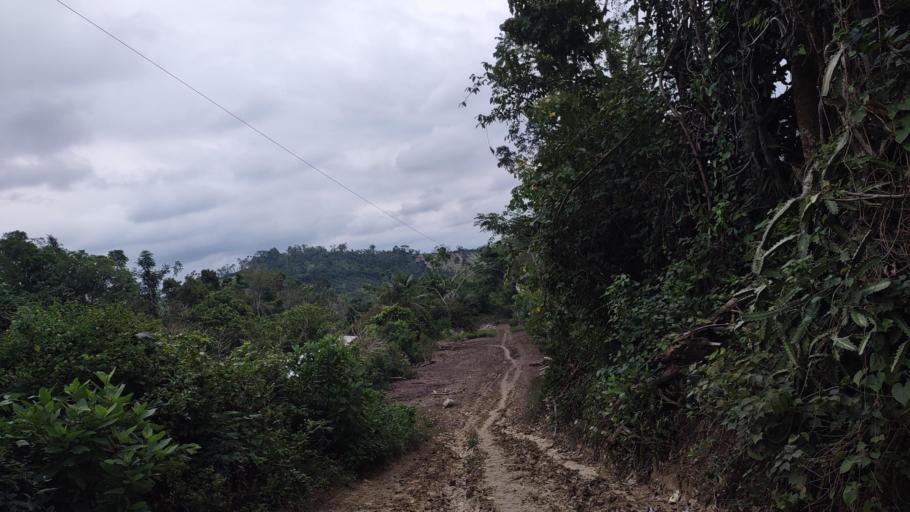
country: MX
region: Veracruz
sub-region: Coatzintla
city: Manuel Maria Contreras
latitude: 20.4111
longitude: -97.4572
